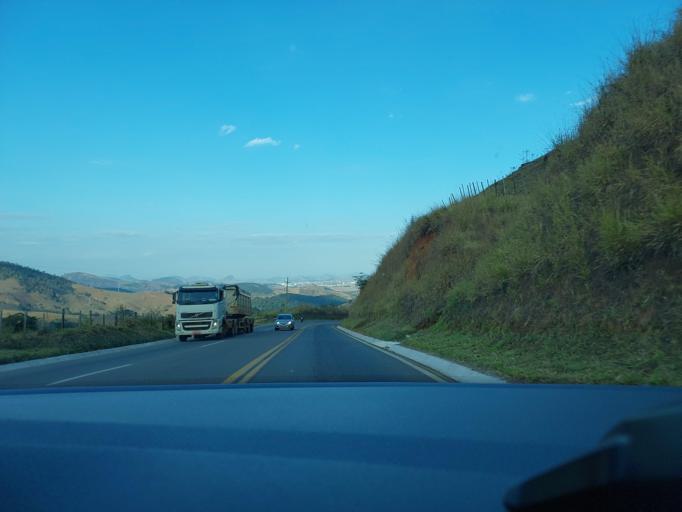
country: BR
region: Minas Gerais
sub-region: Muriae
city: Muriae
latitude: -21.0868
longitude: -42.4872
